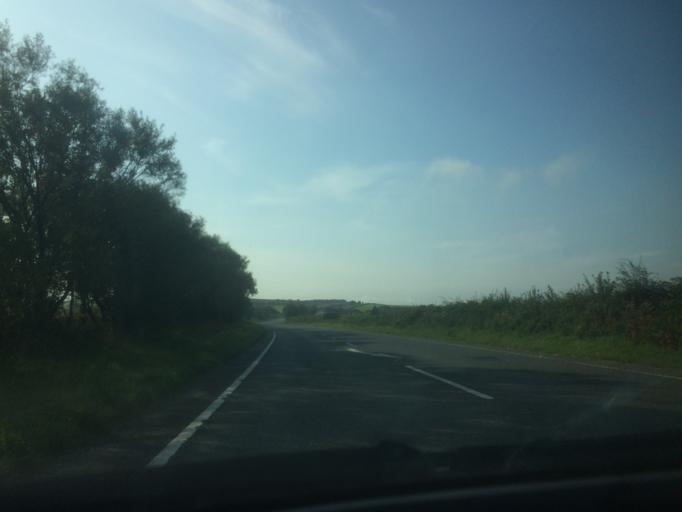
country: GB
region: England
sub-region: Cornwall
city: Callington
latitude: 50.4913
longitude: -4.2895
